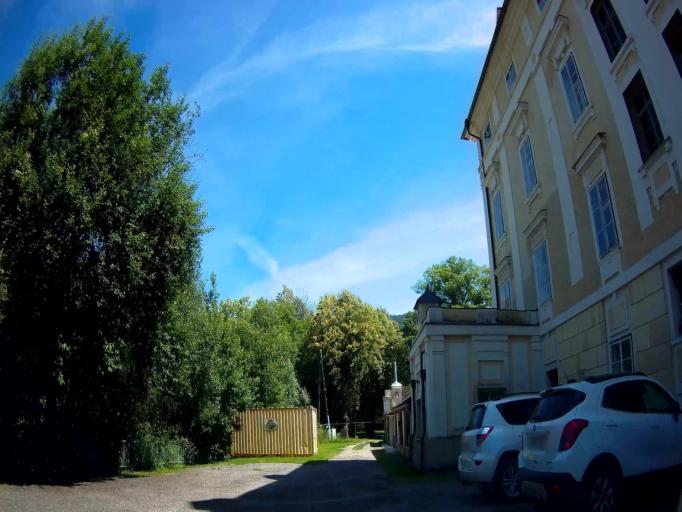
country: AT
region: Carinthia
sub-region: Politischer Bezirk Sankt Veit an der Glan
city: Micheldorf
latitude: 46.8909
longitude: 14.4397
